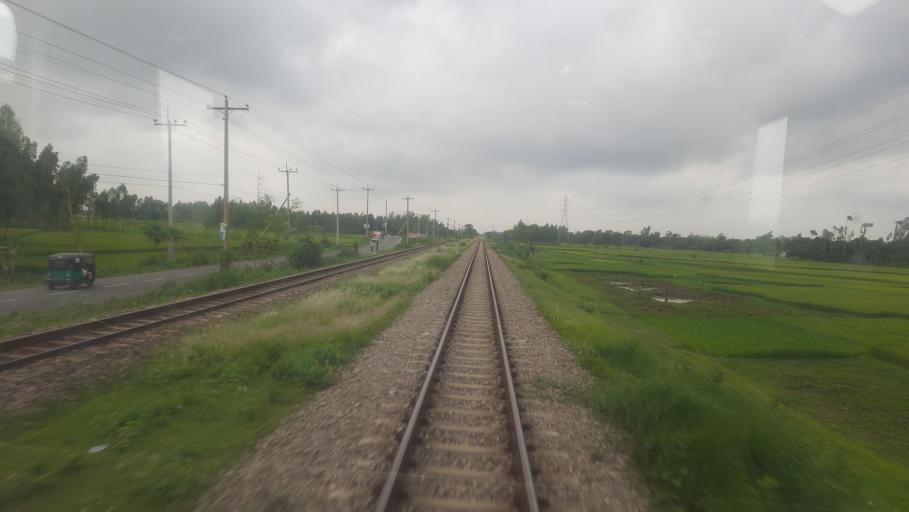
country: BD
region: Dhaka
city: Bhairab Bazar
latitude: 23.9863
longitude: 90.8532
